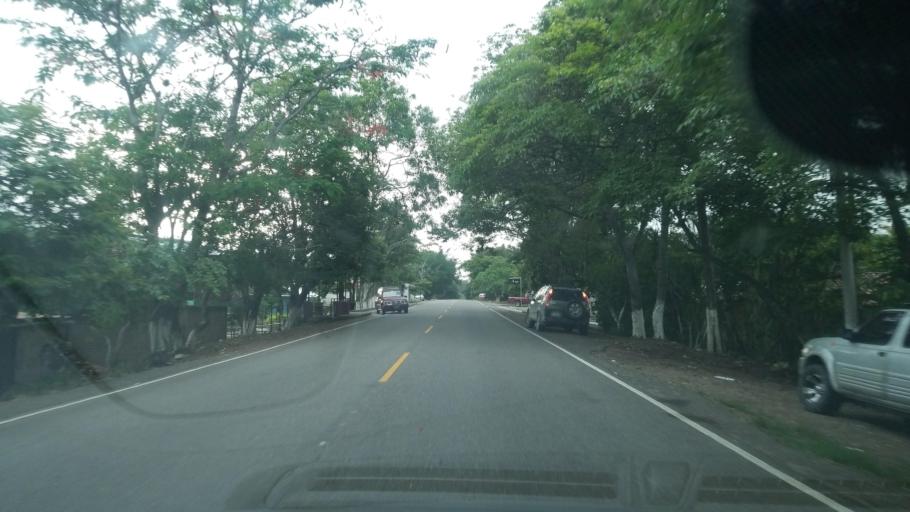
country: HN
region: Ocotepeque
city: Sinuapa
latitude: 14.5104
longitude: -89.2291
